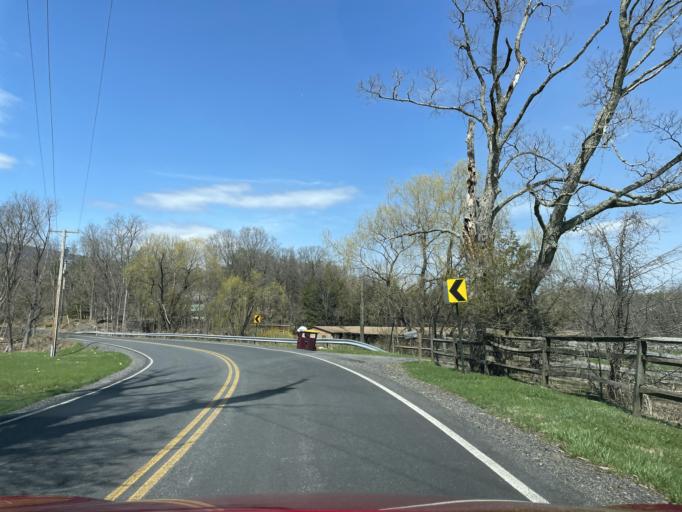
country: US
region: New York
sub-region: Ulster County
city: Manorville
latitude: 42.1172
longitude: -74.0175
